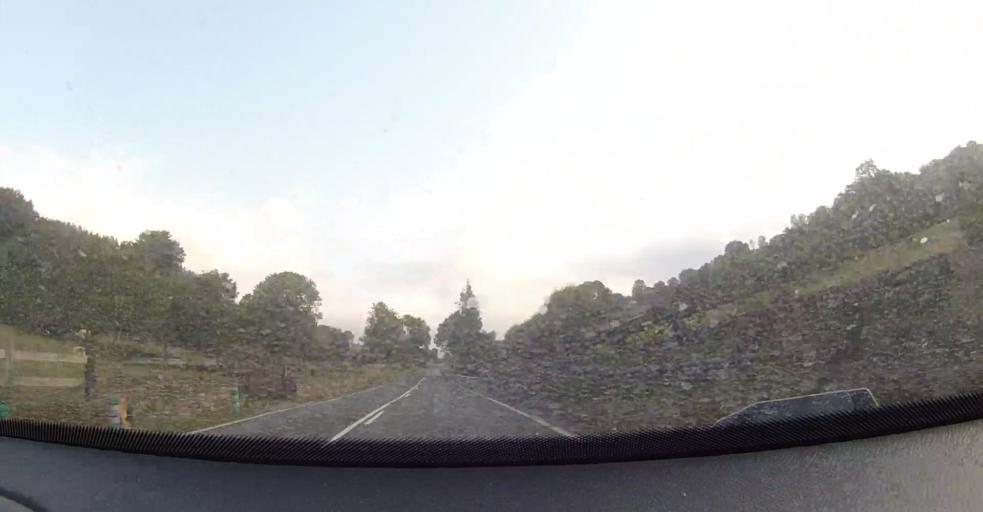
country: ES
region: Basque Country
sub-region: Bizkaia
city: Urrestieta
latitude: 43.2339
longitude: -3.1586
